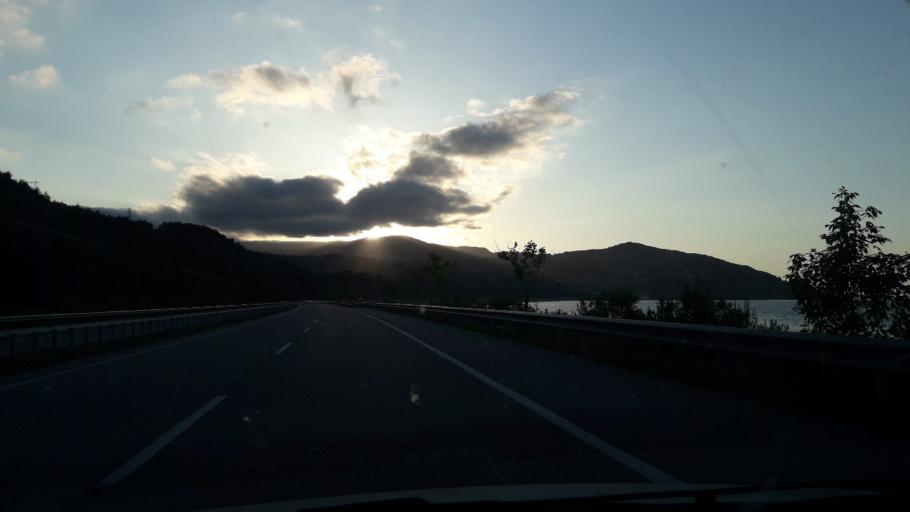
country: TR
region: Sinop
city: Dikmen
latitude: 41.7121
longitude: 35.2880
